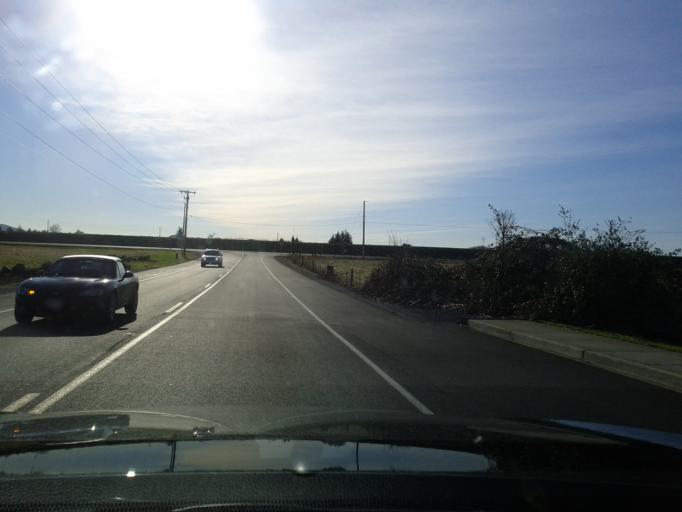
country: US
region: Washington
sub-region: Skagit County
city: Mount Vernon
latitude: 48.4479
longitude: -122.3449
